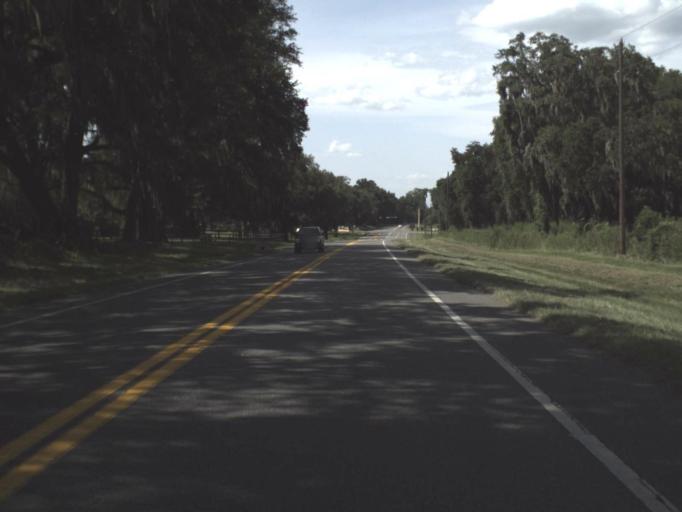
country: US
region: Florida
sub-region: Alachua County
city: High Springs
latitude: 29.9509
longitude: -82.7133
